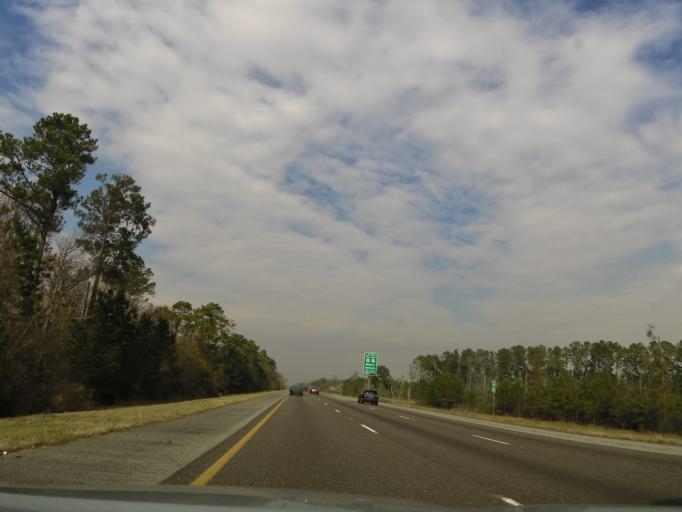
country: US
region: Georgia
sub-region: Liberty County
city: Midway
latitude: 31.7584
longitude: -81.3821
